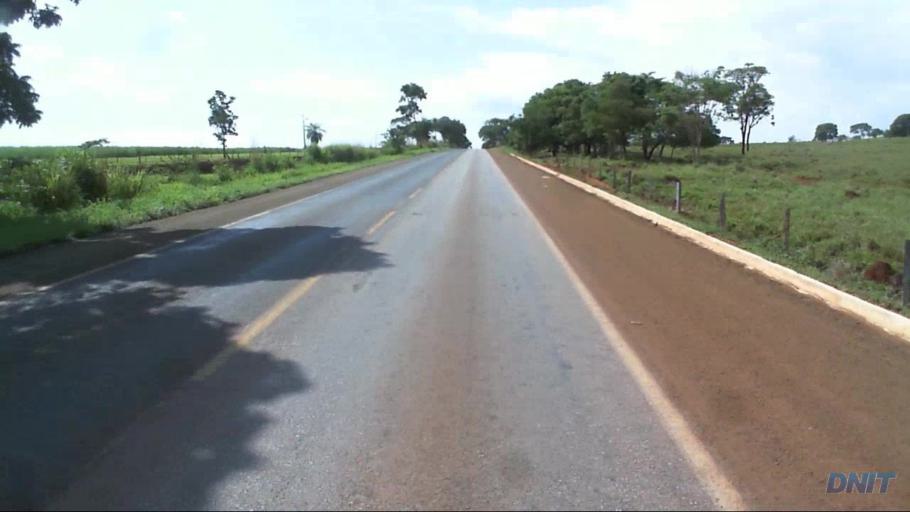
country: BR
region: Goias
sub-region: Barro Alto
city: Barro Alto
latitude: -15.0167
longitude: -48.8989
